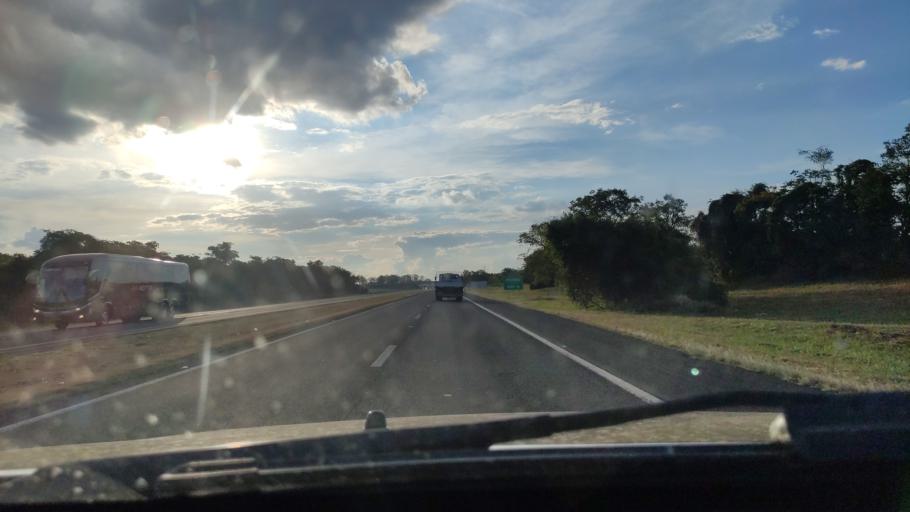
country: BR
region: Sao Paulo
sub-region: Rancharia
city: Rancharia
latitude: -22.4660
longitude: -50.9555
